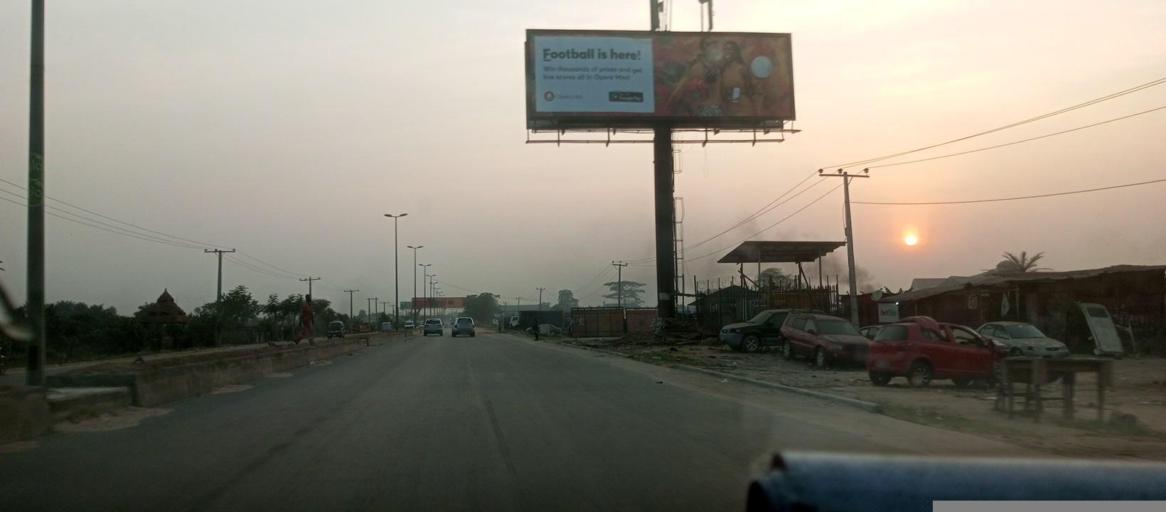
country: NG
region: Rivers
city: Emuoha
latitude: 4.9315
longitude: 7.0026
